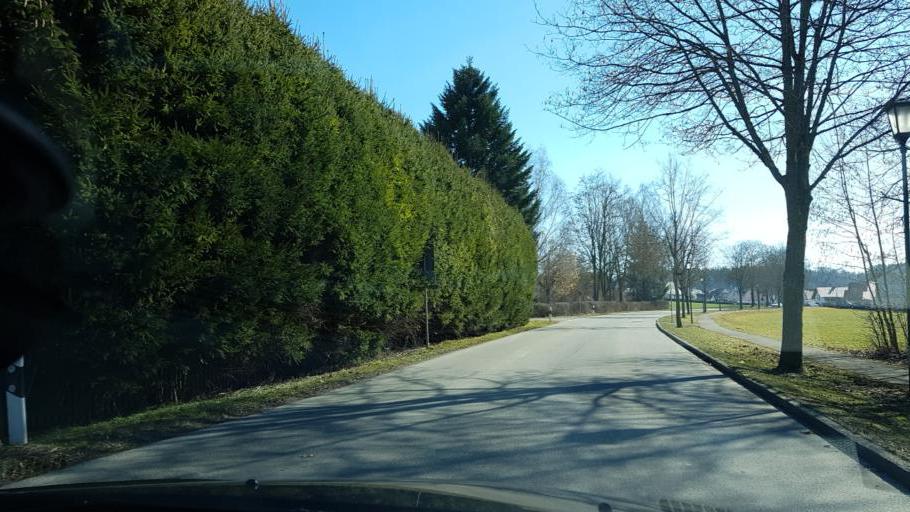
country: DE
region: Bavaria
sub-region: Upper Bavaria
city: Oberschweinbach
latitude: 48.2379
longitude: 11.1565
